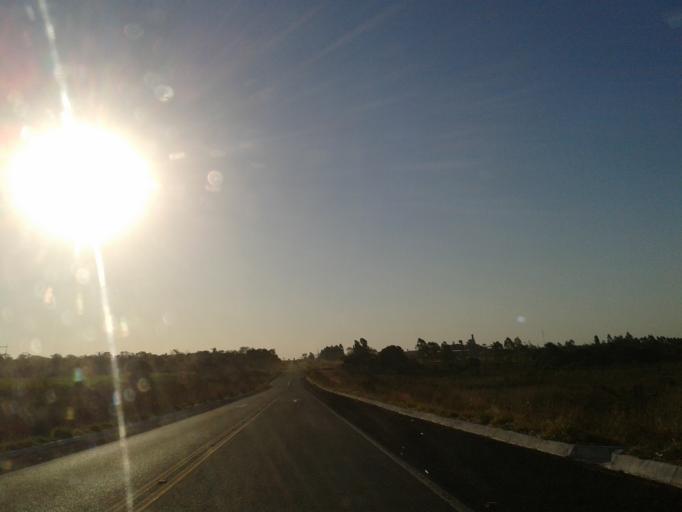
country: BR
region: Minas Gerais
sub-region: Santa Vitoria
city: Santa Vitoria
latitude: -19.0794
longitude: -50.3609
